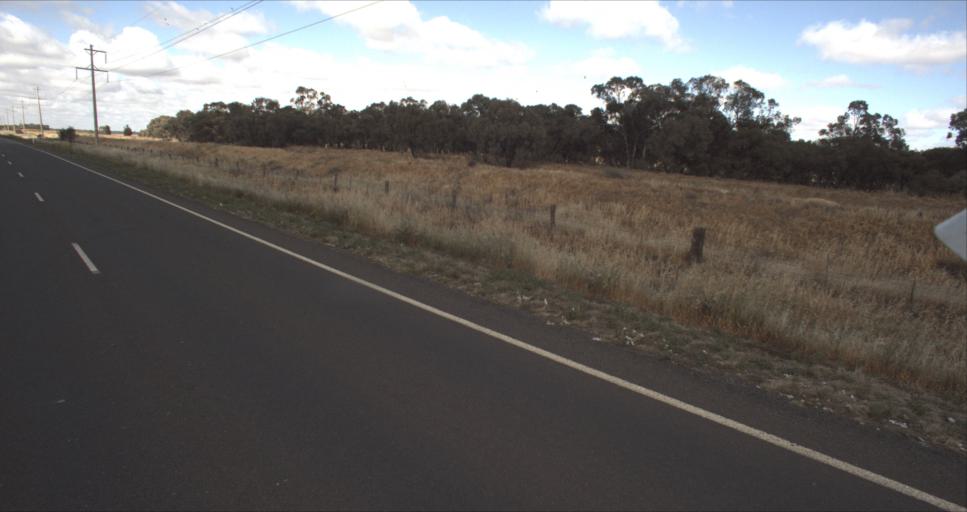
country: AU
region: New South Wales
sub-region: Murrumbidgee Shire
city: Darlington Point
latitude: -34.5430
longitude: 146.1718
